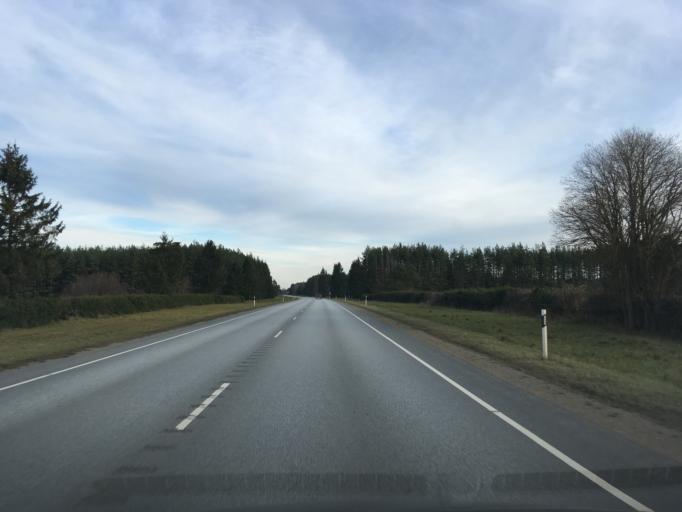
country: EE
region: Laeaene-Virumaa
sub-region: Viru-Nigula vald
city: Kunda
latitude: 59.3922
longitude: 26.6208
